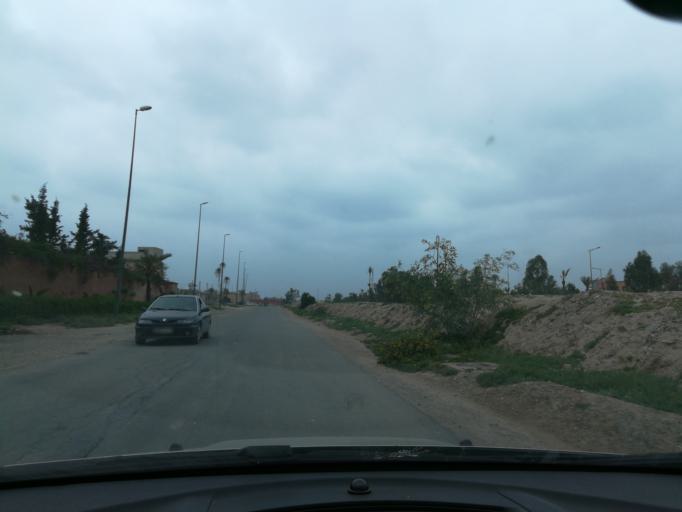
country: MA
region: Marrakech-Tensift-Al Haouz
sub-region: Marrakech
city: Marrakesh
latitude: 31.6534
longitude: -7.9848
